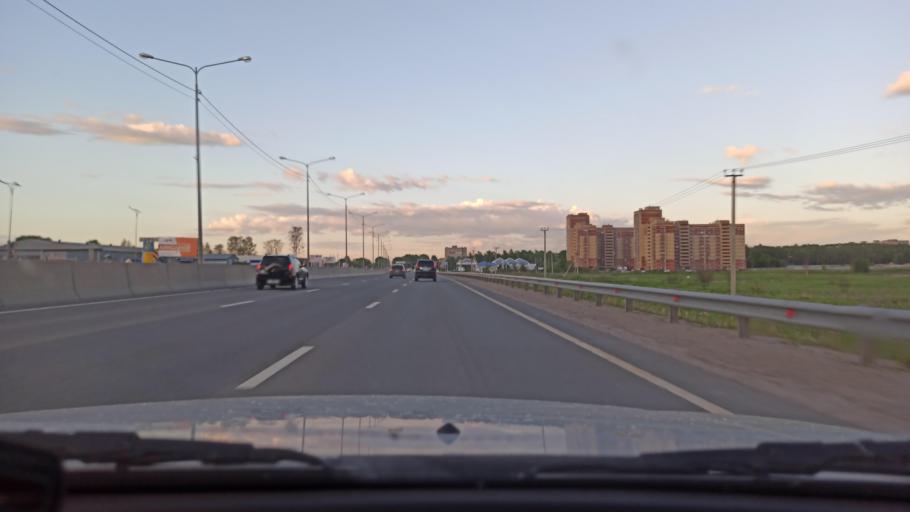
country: RU
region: Vologda
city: Vologda
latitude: 59.2147
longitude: 39.7995
